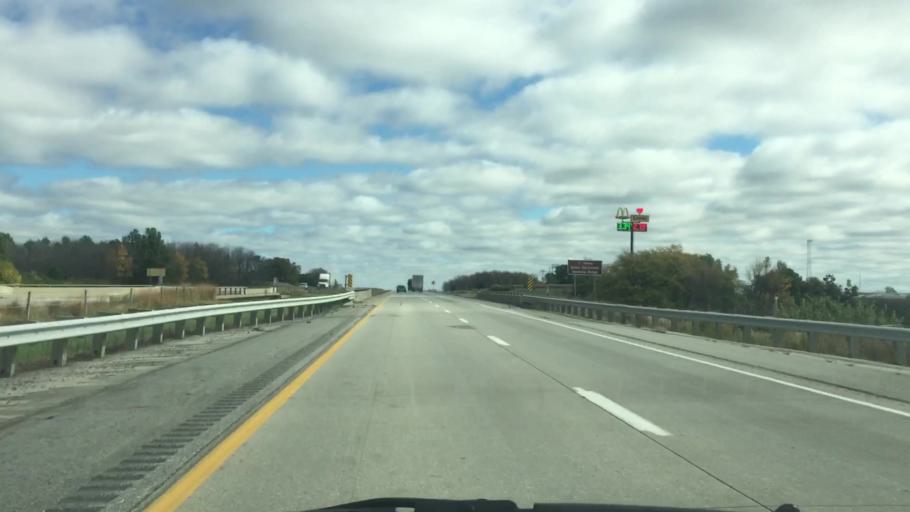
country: US
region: Iowa
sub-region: Jasper County
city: Newton
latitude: 41.6825
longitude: -93.0007
